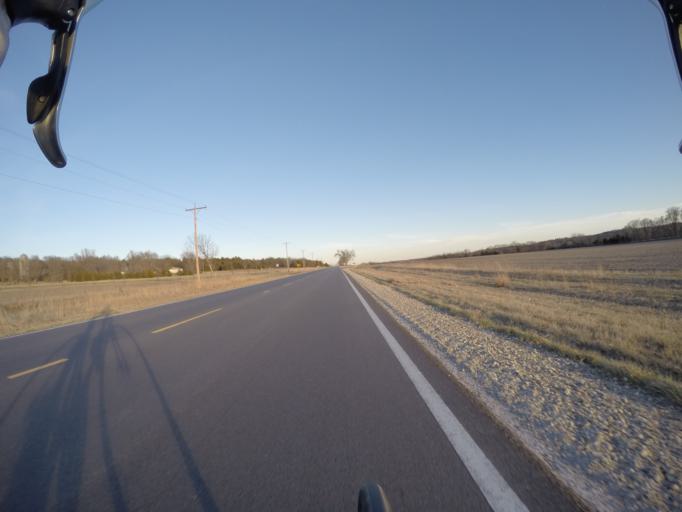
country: US
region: Kansas
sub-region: Riley County
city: Ogden
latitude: 39.2094
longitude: -96.6773
